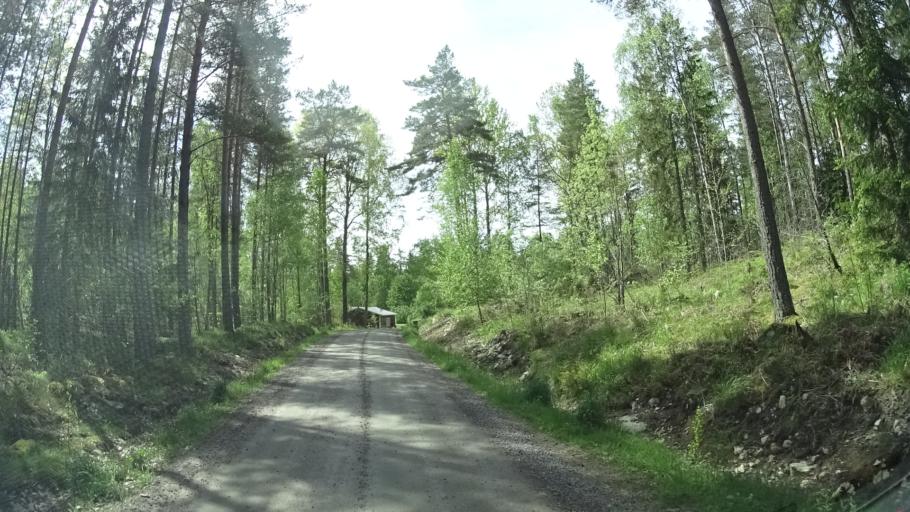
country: SE
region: OEstergoetland
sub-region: Finspangs Kommun
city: Finspang
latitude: 58.7626
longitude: 15.8341
